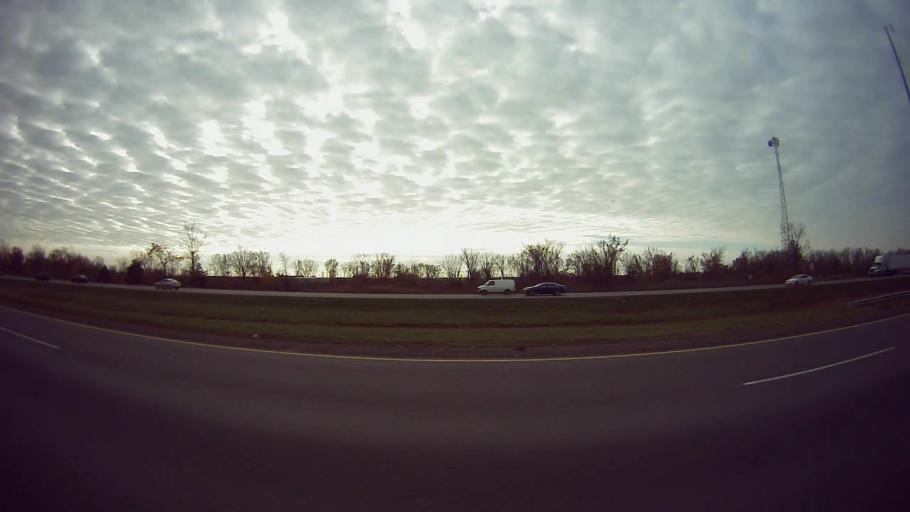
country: US
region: Michigan
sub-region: Wayne County
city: Romulus
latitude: 42.2291
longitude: -83.3829
